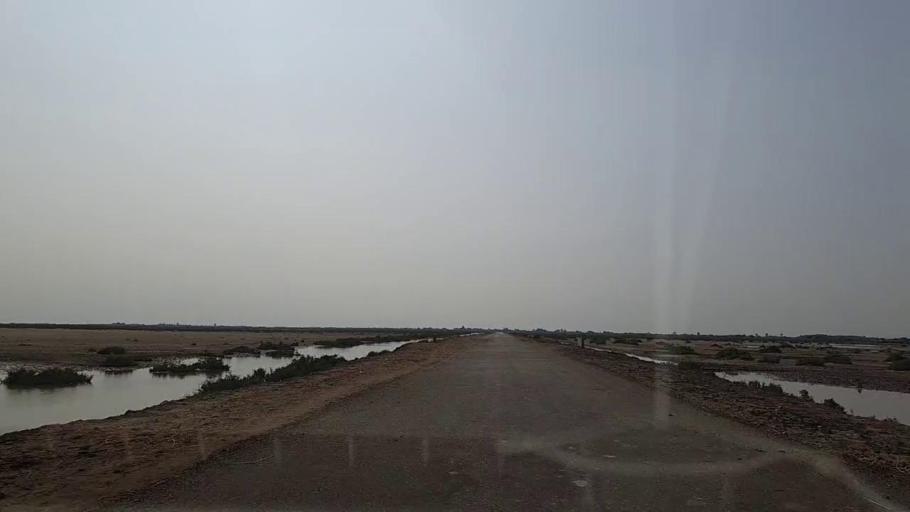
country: PK
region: Sindh
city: Chuhar Jamali
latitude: 24.2085
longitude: 67.8579
